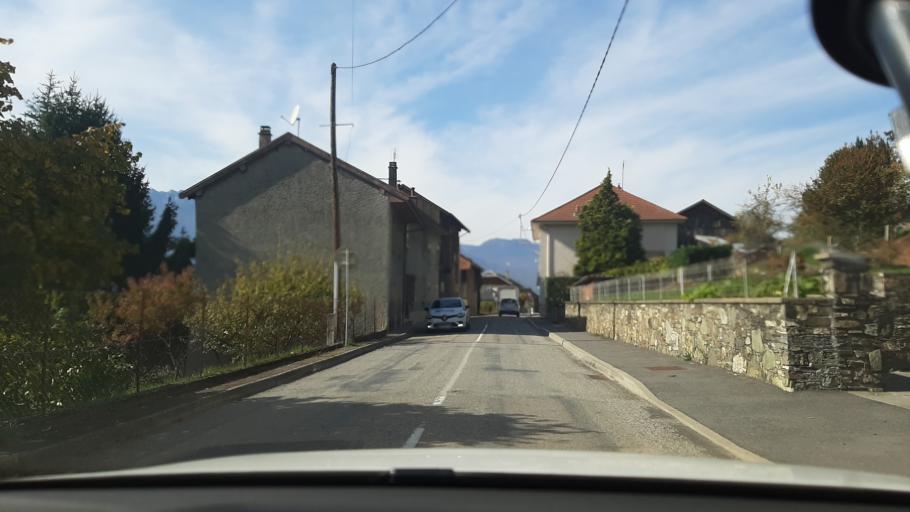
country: FR
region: Rhone-Alpes
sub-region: Departement de la Savoie
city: La Rochette
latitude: 45.4478
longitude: 6.0698
